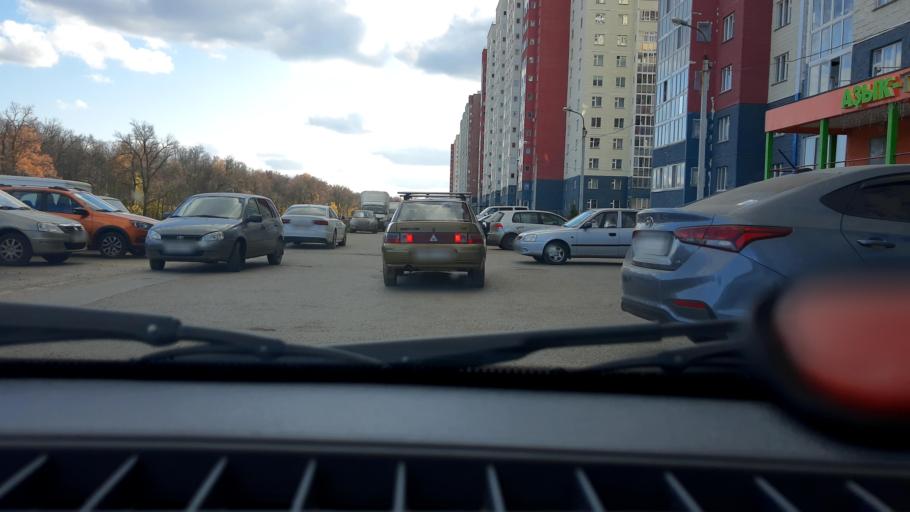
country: RU
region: Bashkortostan
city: Ufa
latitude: 54.7858
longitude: 56.1383
